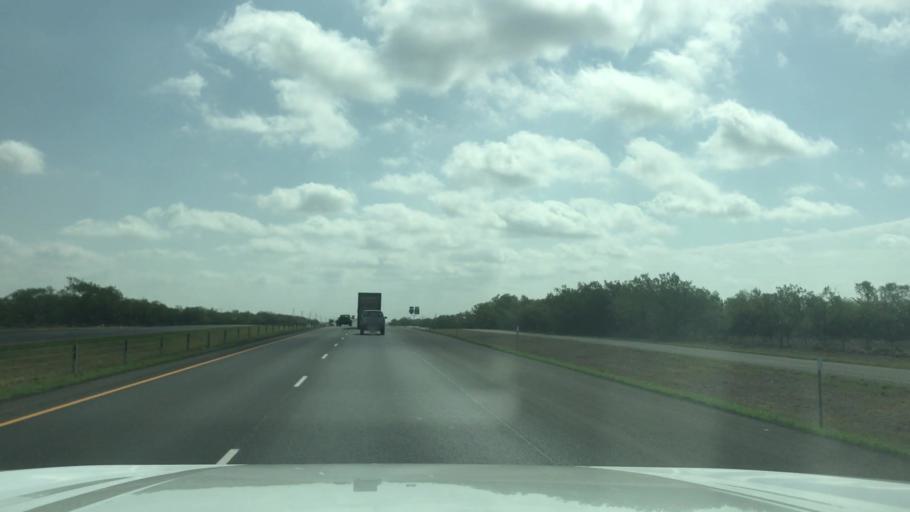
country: US
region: Texas
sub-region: Taylor County
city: Merkel
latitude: 32.4927
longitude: -100.1575
